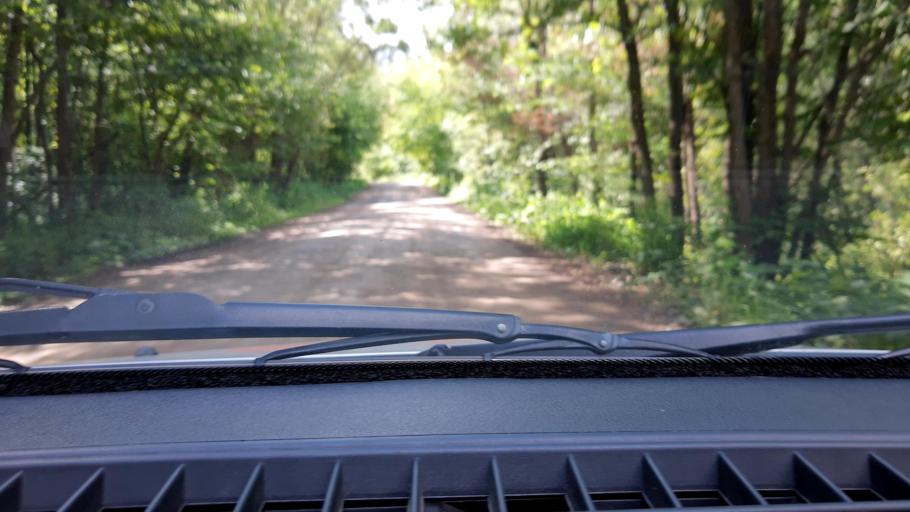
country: RU
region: Bashkortostan
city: Ufa
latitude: 54.6845
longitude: 56.0597
